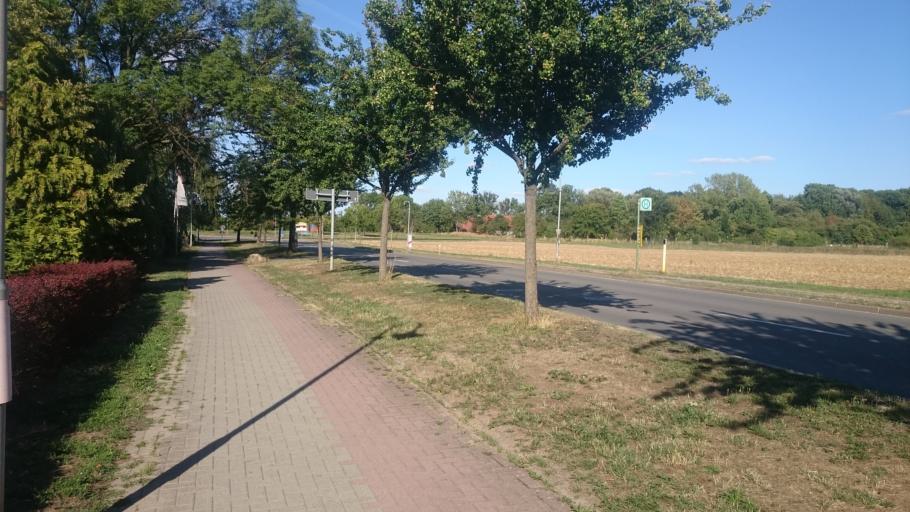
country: DE
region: Saxony-Anhalt
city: Gernrode
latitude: 51.7290
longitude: 11.1489
